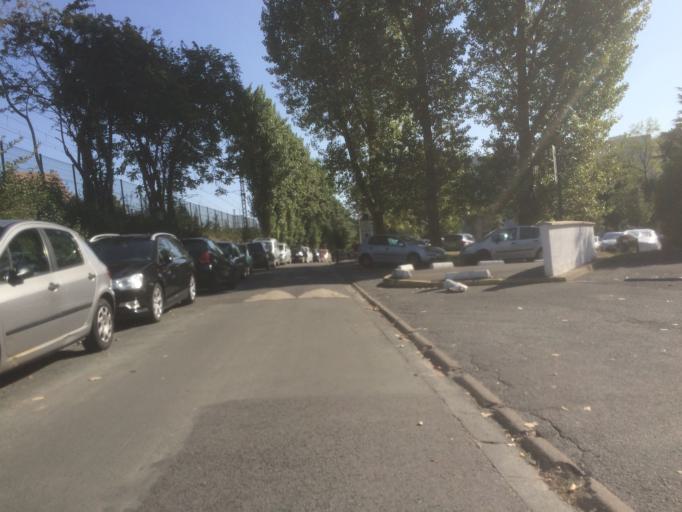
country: FR
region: Ile-de-France
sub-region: Departement de l'Essonne
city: Longjumeau
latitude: 48.6905
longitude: 2.3157
